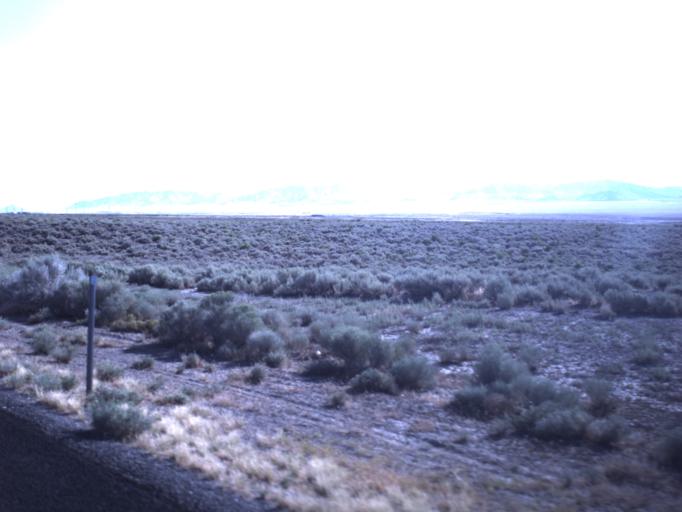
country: US
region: Utah
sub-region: Beaver County
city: Milford
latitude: 38.4480
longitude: -113.0082
